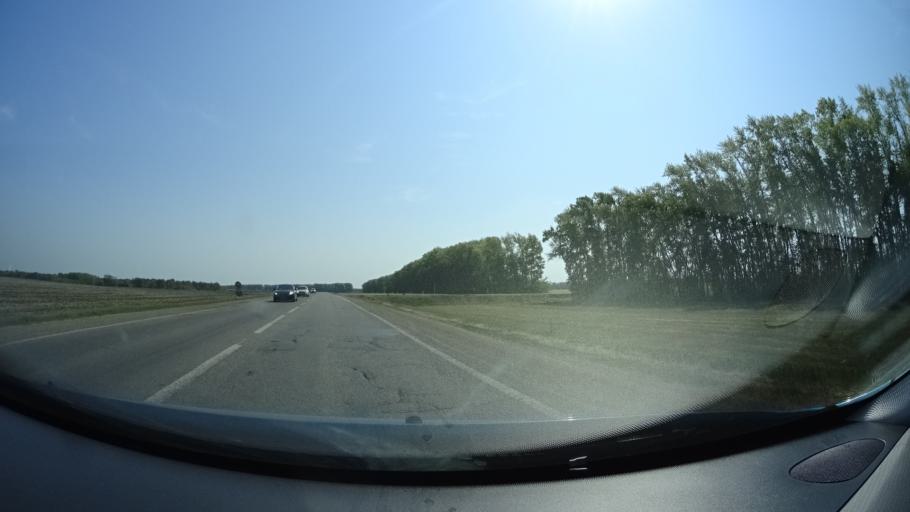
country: RU
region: Bashkortostan
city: Karmaskaly
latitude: 54.3897
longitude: 56.1262
